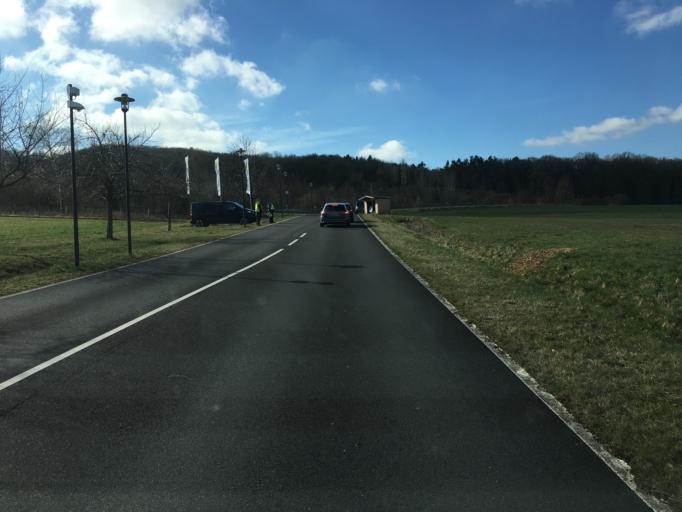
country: DE
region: North Rhine-Westphalia
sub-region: Regierungsbezirk Koln
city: Mechernich
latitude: 50.6191
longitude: 6.6323
